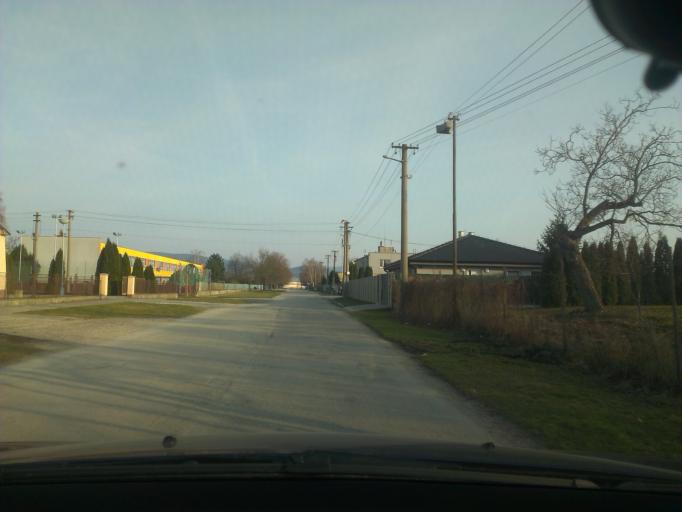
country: SK
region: Trnavsky
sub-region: Okres Trnava
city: Piestany
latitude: 48.6569
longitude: 17.8471
